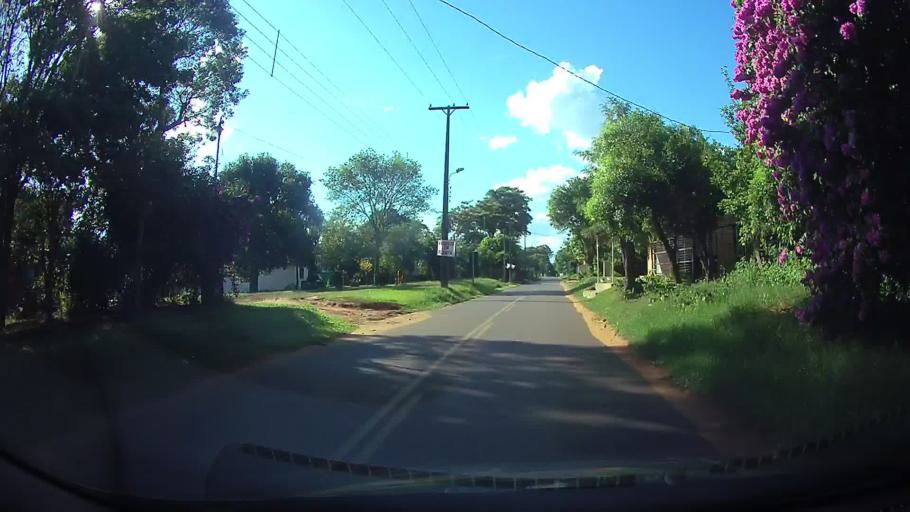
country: PY
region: Central
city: Aregua
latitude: -25.3597
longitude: -57.3864
